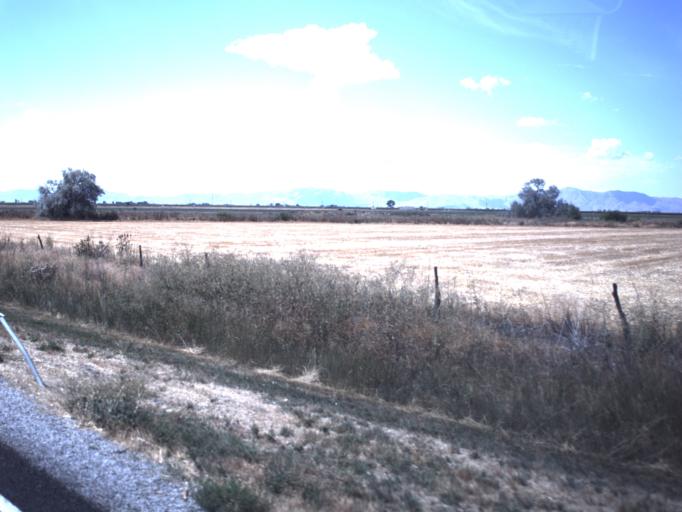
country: US
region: Utah
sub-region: Box Elder County
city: Honeyville
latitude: 41.5955
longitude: -112.1280
